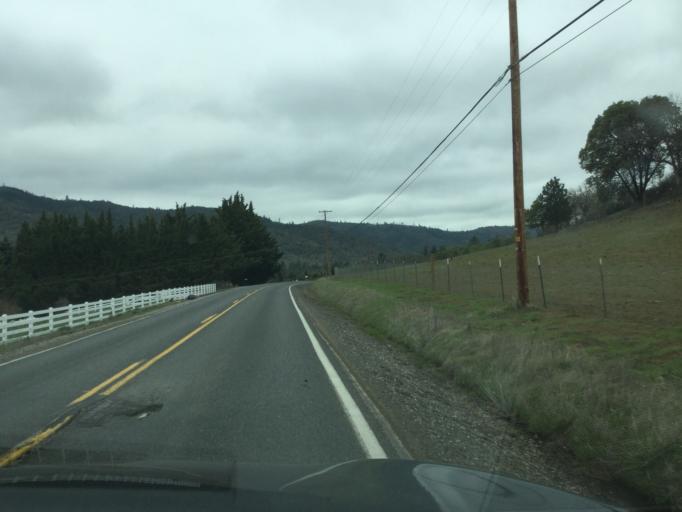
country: US
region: Oregon
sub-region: Jackson County
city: Gold Hill
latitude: 42.3984
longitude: -123.0165
